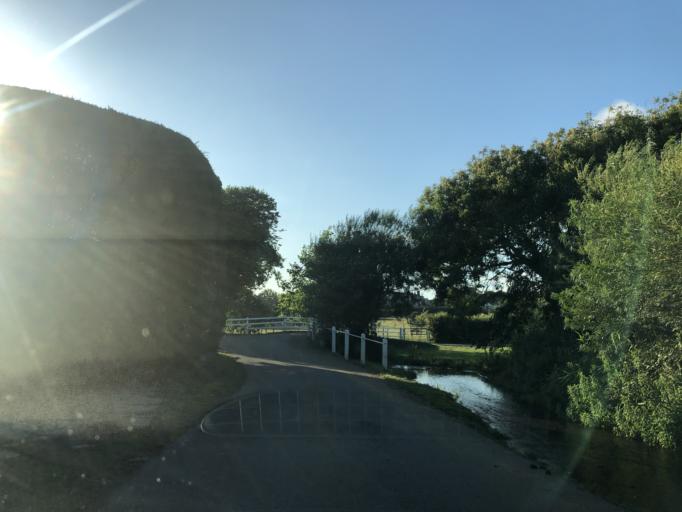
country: GB
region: England
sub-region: Isle of Wight
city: Shalfleet
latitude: 50.6401
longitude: -1.3928
